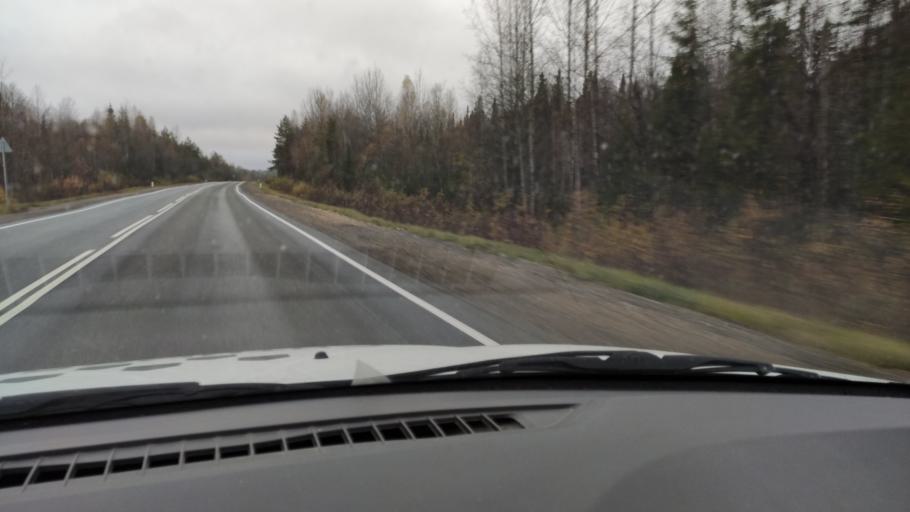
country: RU
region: Kirov
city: Omutninsk
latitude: 58.7018
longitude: 52.1122
